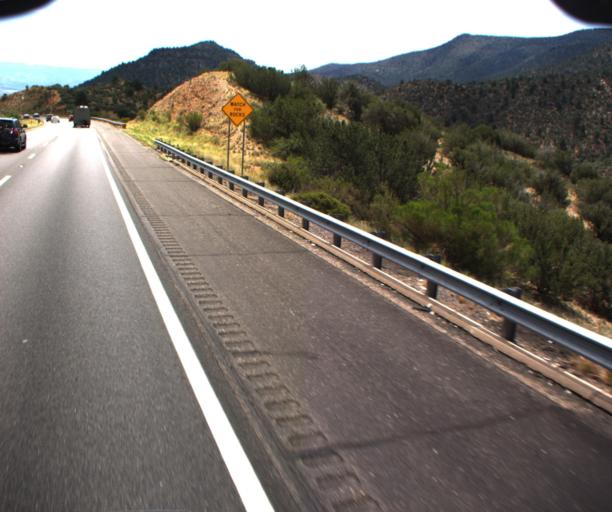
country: US
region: Arizona
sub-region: Yavapai County
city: Camp Verde
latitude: 34.5373
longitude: -111.9219
